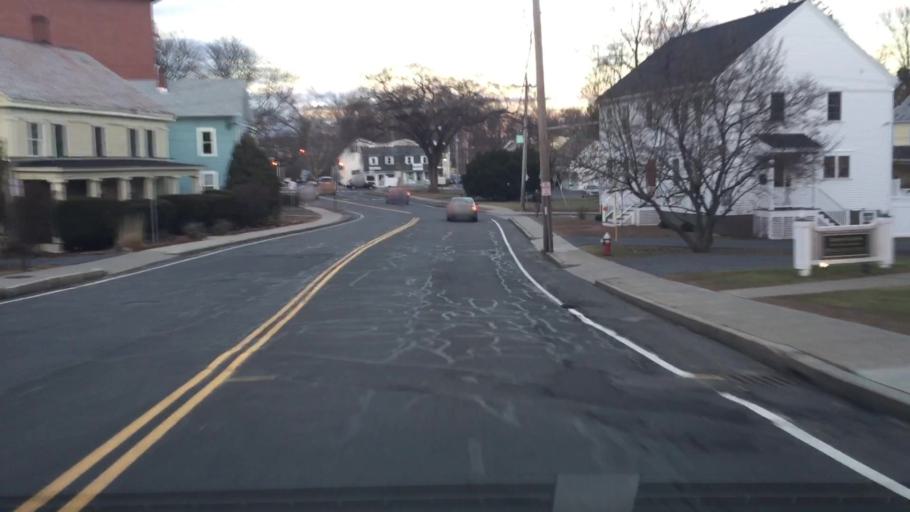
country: US
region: Massachusetts
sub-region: Hampshire County
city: Northampton
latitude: 42.3151
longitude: -72.6327
